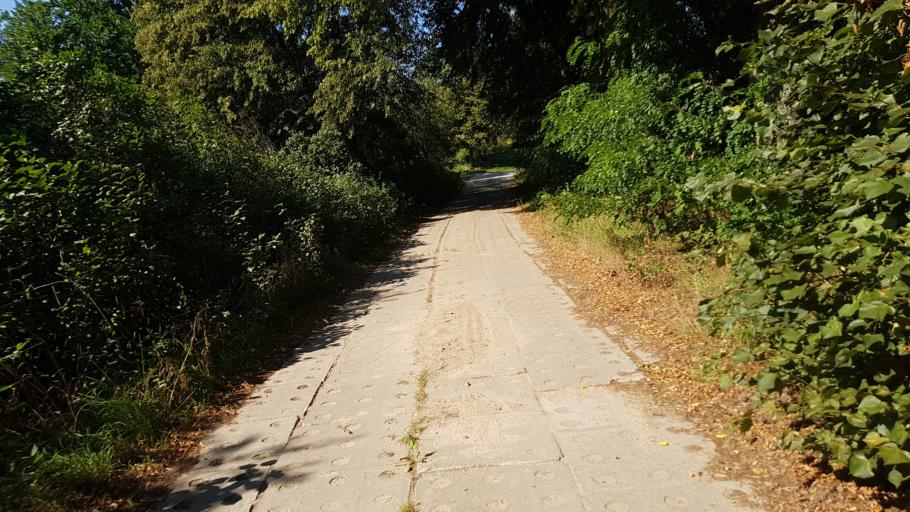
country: PL
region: West Pomeranian Voivodeship
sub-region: Powiat gryfinski
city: Gryfino
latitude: 53.1719
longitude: 14.4713
